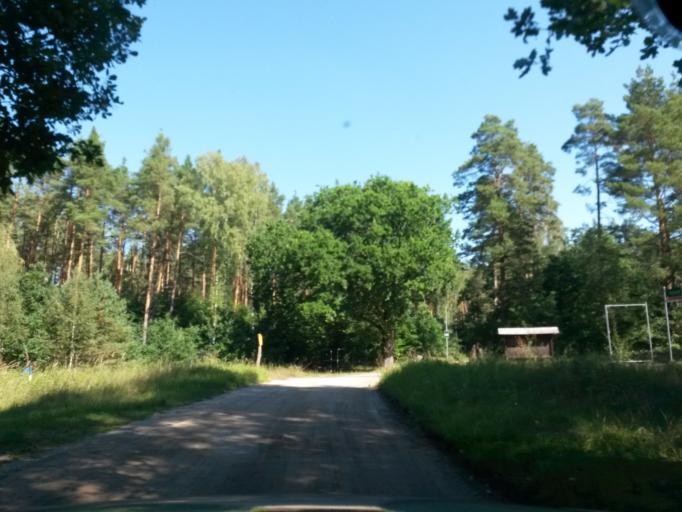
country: DE
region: Brandenburg
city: Lychen
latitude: 53.1521
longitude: 13.3977
